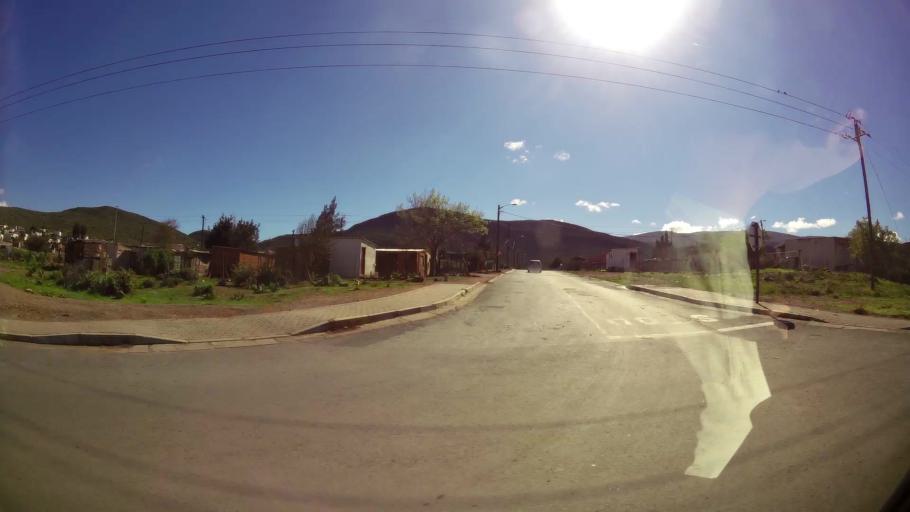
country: ZA
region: Western Cape
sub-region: Cape Winelands District Municipality
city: Ashton
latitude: -33.7692
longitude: 20.1450
